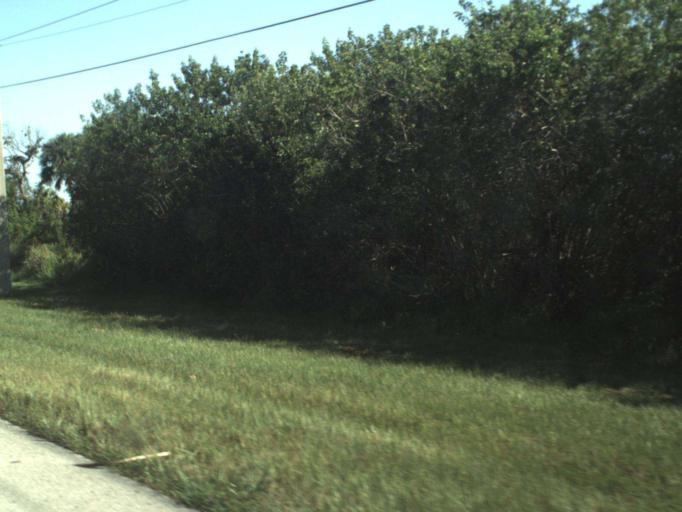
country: US
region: Florida
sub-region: Indian River County
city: Vero Beach
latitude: 27.6618
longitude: -80.3873
